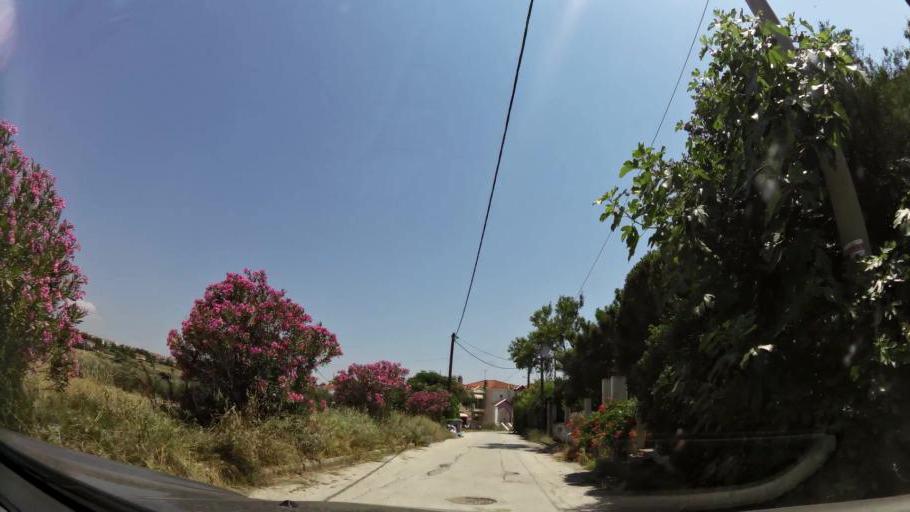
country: GR
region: Central Macedonia
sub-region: Nomos Thessalonikis
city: Plagiari
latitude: 40.4720
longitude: 22.9614
